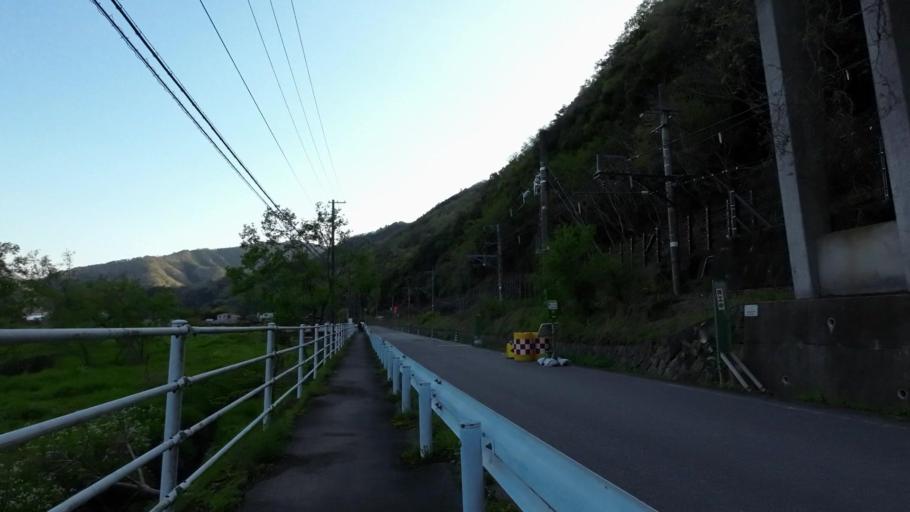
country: JP
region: Hyogo
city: Toyooka
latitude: 35.3794
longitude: 134.8122
